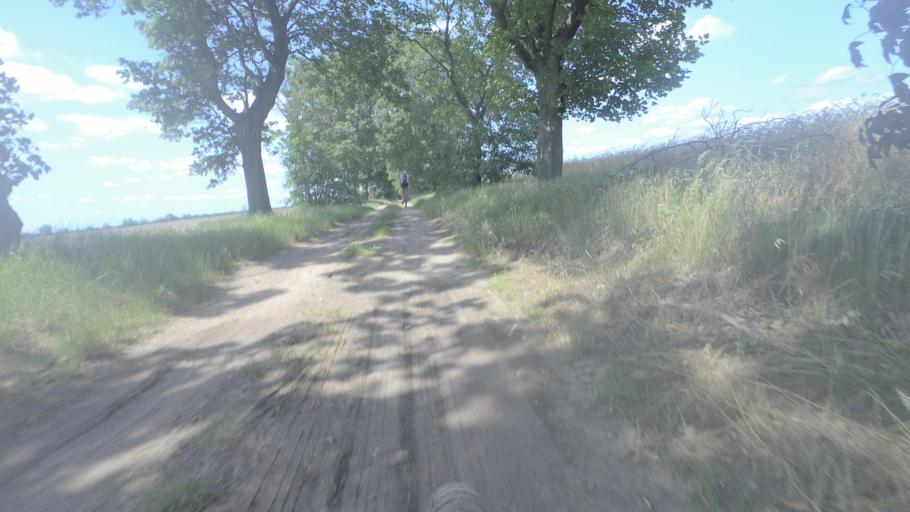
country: DE
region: Brandenburg
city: Am Mellensee
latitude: 52.2423
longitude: 13.3615
